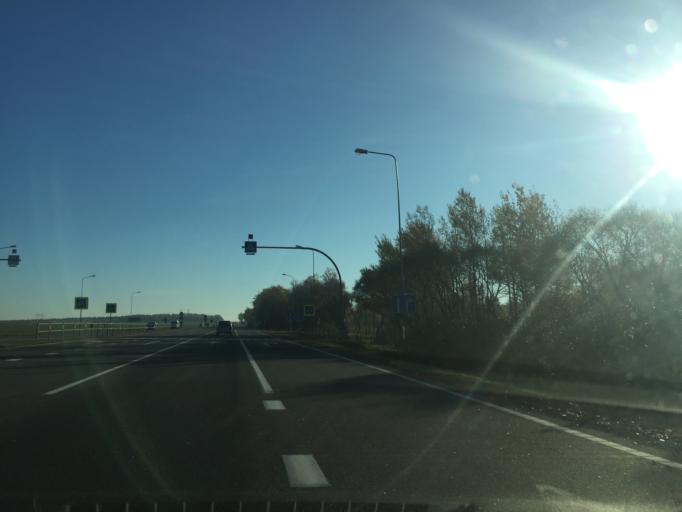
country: BY
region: Minsk
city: Smilavichy
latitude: 53.7636
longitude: 28.0905
